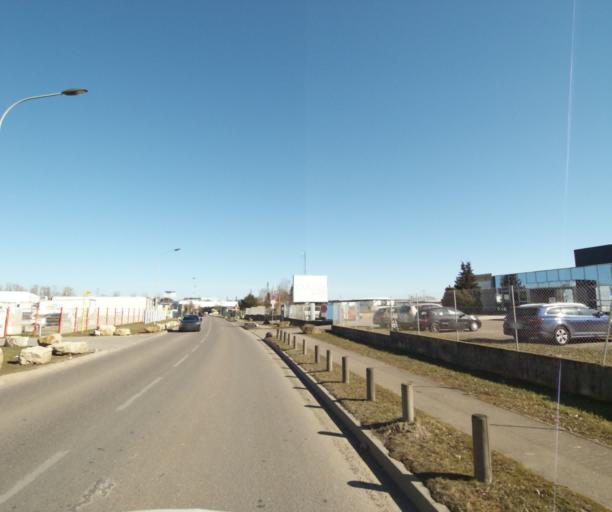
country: FR
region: Lorraine
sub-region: Departement de Meurthe-et-Moselle
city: Fleville-devant-Nancy
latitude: 48.6137
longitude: 6.2008
